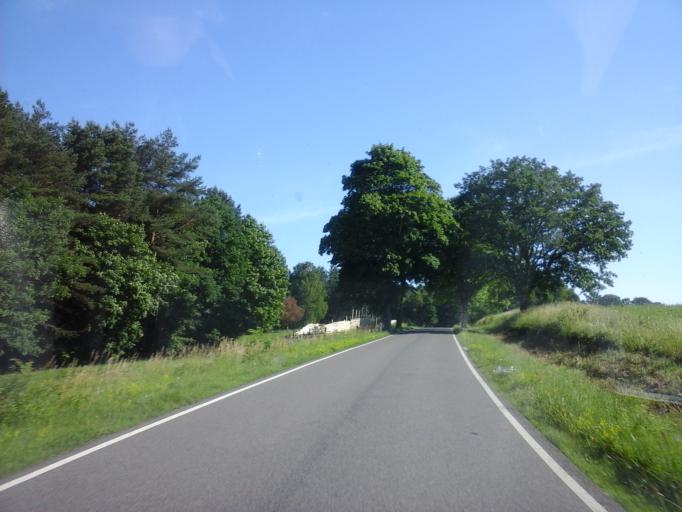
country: PL
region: West Pomeranian Voivodeship
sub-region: Powiat drawski
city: Zlocieniec
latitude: 53.6132
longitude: 15.9215
